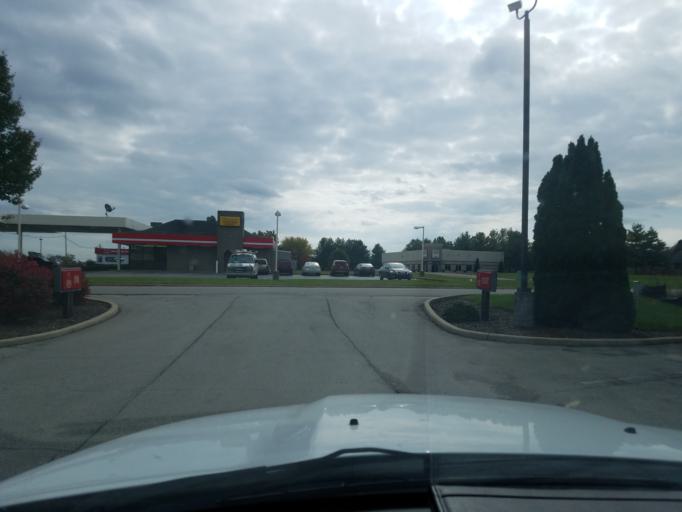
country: US
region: Kentucky
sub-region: Bullitt County
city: Mount Washington
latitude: 38.0607
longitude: -85.5465
